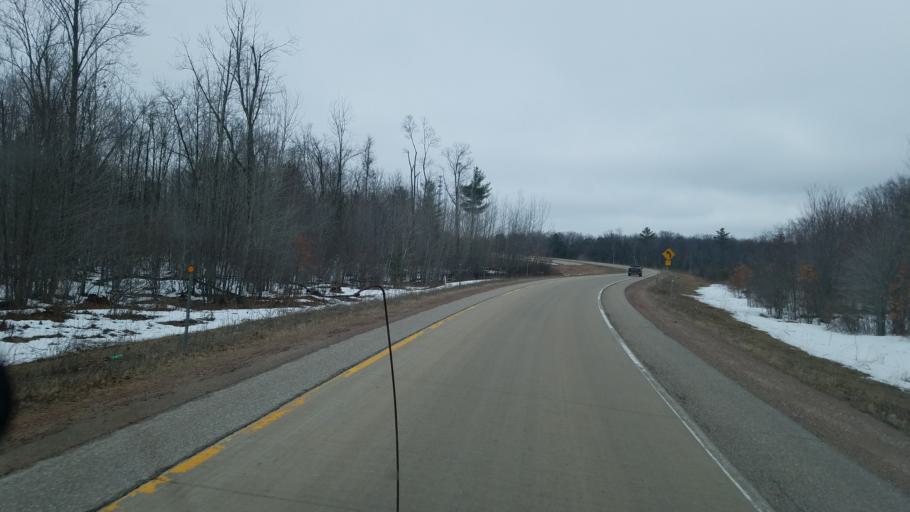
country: US
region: Wisconsin
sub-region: Portage County
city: Stevens Point
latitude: 44.5906
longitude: -89.6089
